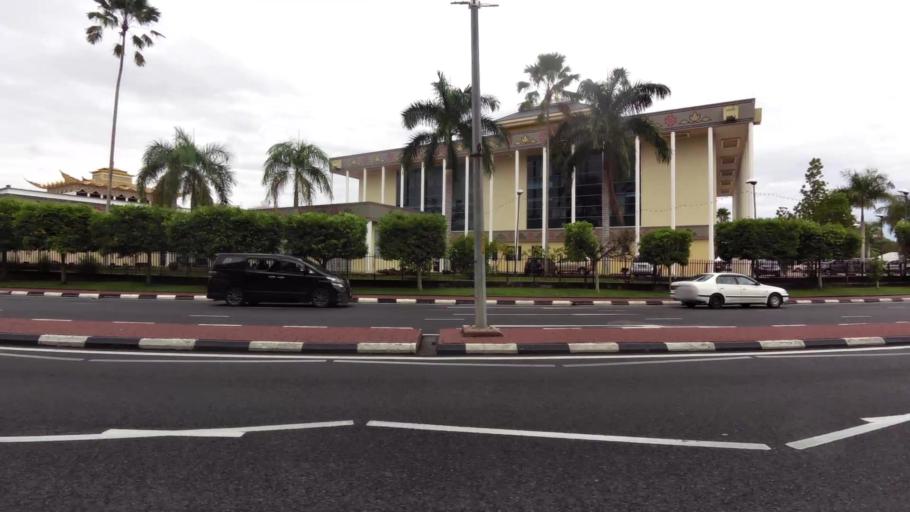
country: BN
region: Brunei and Muara
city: Bandar Seri Begawan
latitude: 4.8934
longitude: 114.9434
